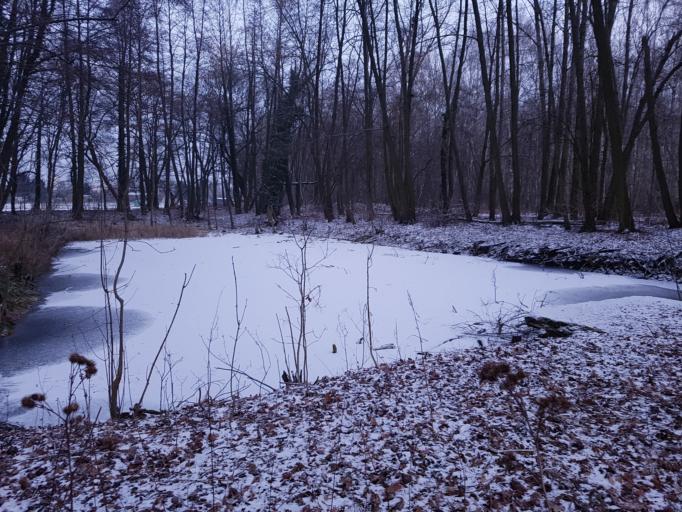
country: DE
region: Brandenburg
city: Finsterwalde
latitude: 51.6296
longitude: 13.7214
